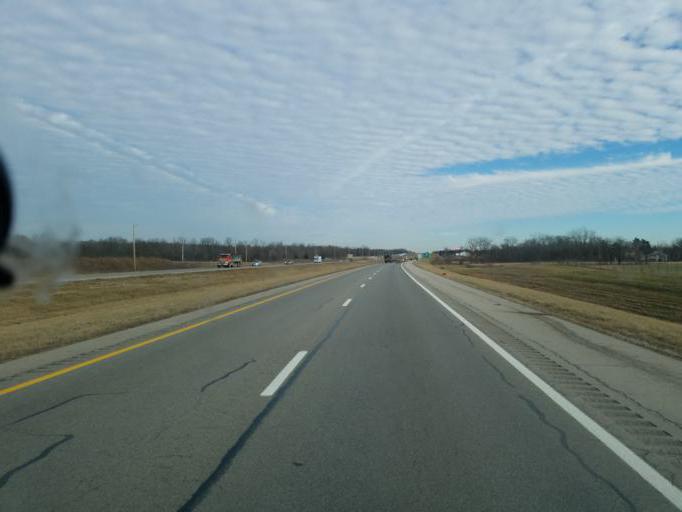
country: US
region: Ohio
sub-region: Franklin County
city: New Albany
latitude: 40.0808
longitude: -82.7418
